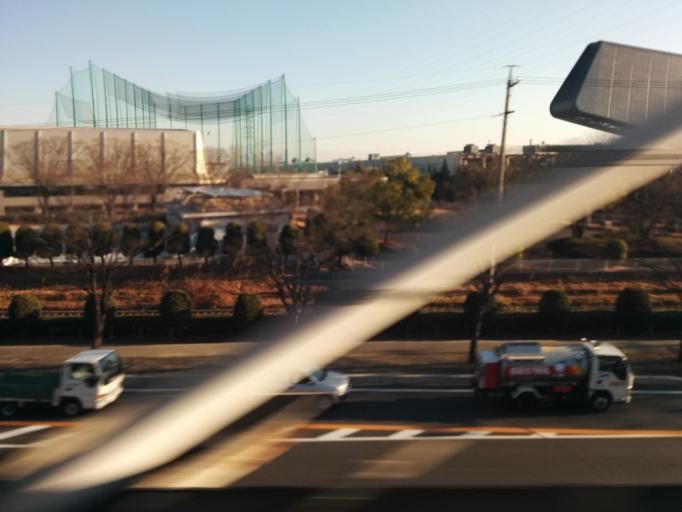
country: JP
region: Gifu
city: Ogaki
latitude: 35.3313
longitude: 136.6678
